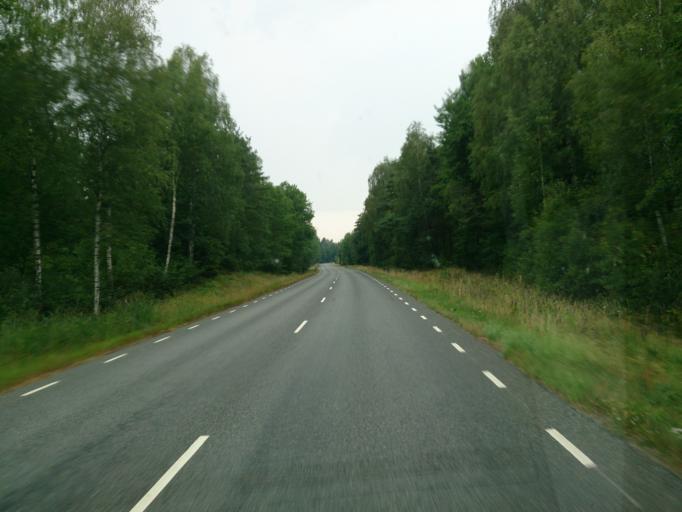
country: SE
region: Skane
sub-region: Kristianstads Kommun
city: Tollarp
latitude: 56.1893
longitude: 14.2276
